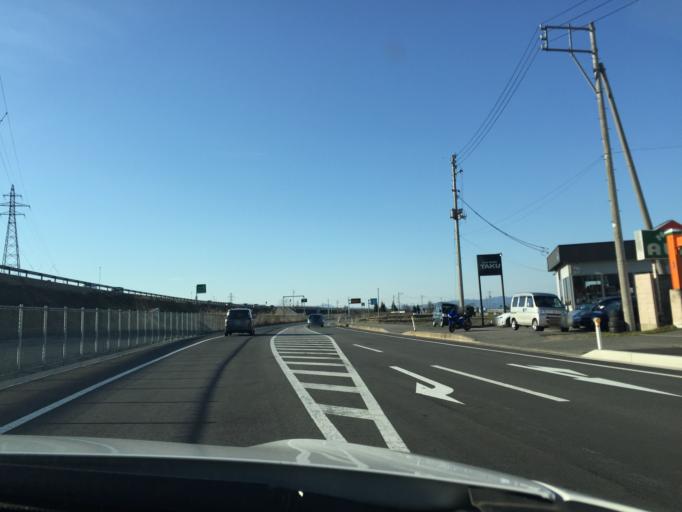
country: JP
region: Yamagata
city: Yonezawa
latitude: 37.9472
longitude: 140.1165
